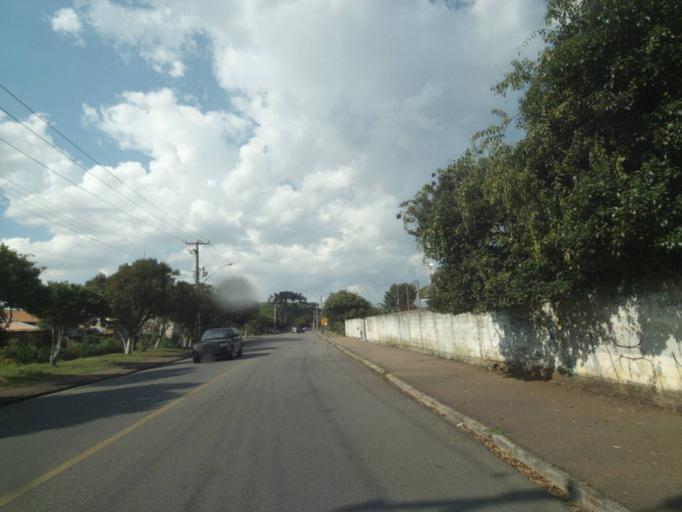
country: BR
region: Parana
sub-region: Sao Jose Dos Pinhais
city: Sao Jose dos Pinhais
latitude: -25.5287
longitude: -49.2702
